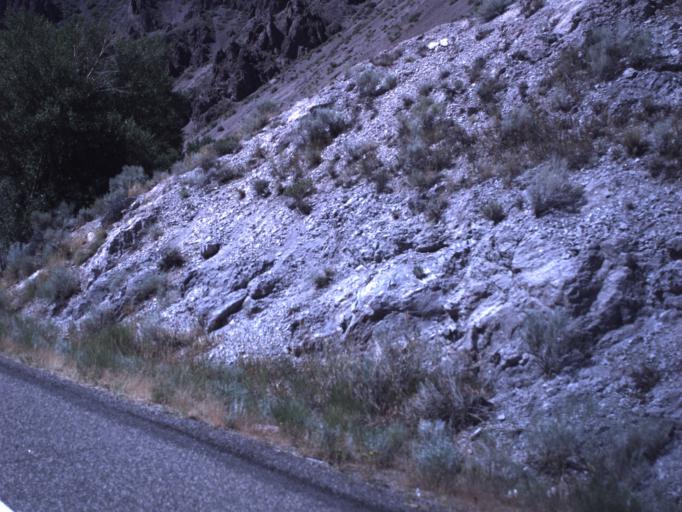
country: US
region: Utah
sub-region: Sevier County
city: Monroe
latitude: 38.5020
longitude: -112.2579
